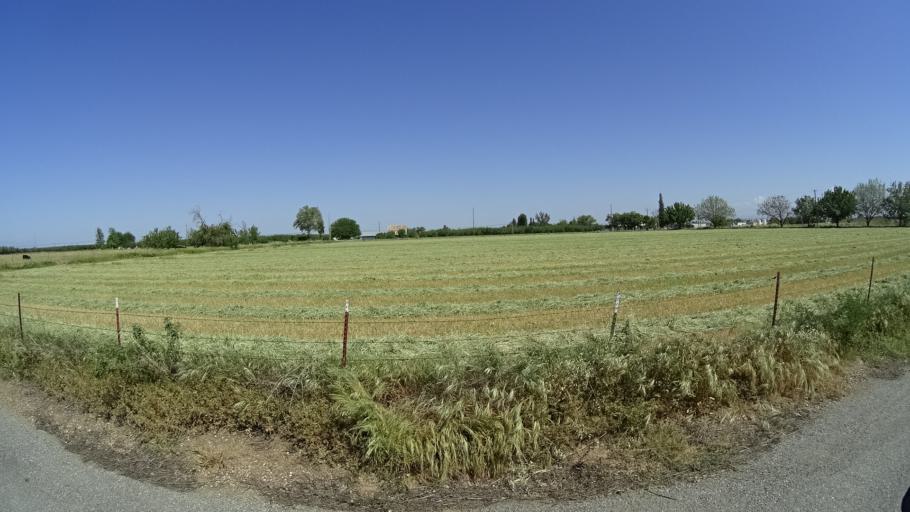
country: US
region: California
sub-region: Glenn County
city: Orland
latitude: 39.7664
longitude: -122.1612
